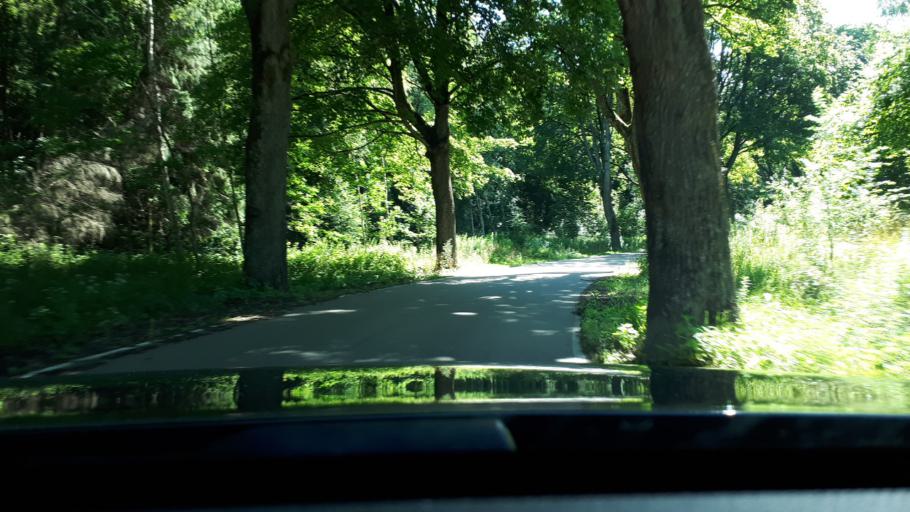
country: PL
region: Warmian-Masurian Voivodeship
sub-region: Powiat ostrodzki
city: Ostroda
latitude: 53.6849
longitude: 20.0656
